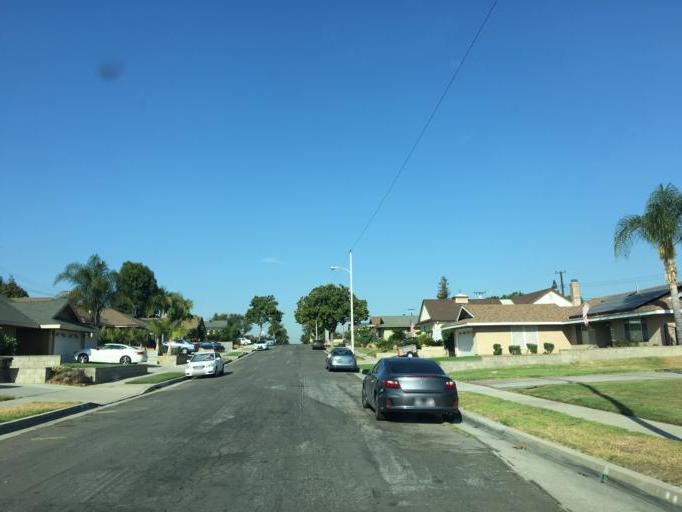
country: US
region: California
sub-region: Los Angeles County
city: Avocado Heights
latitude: 34.0401
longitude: -118.0046
